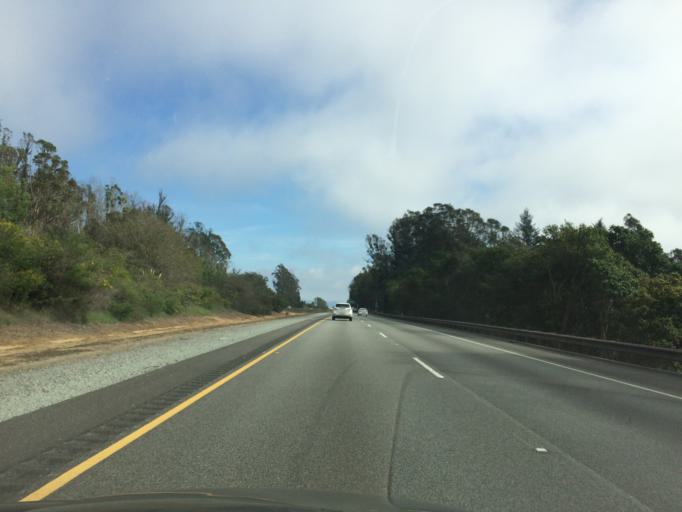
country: US
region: California
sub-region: Santa Cruz County
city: Aptos Hills-Larkin Valley
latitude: 36.9370
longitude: -121.8296
